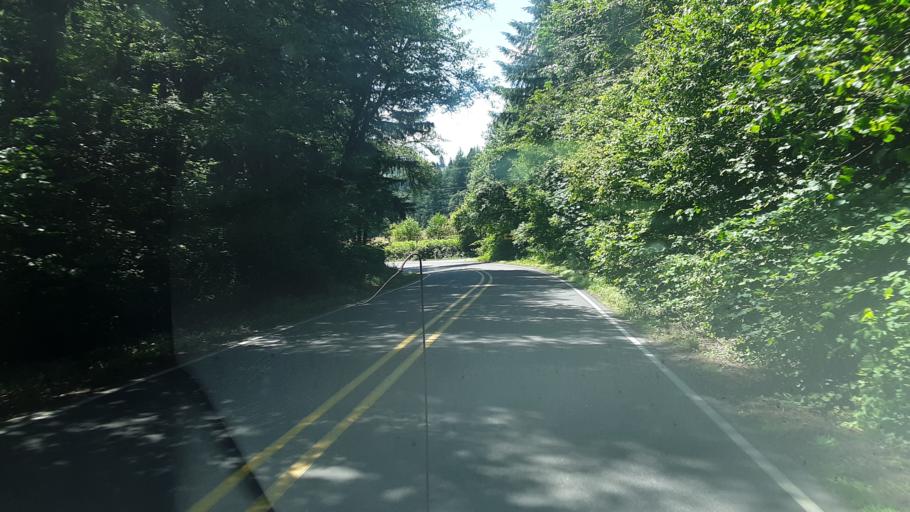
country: US
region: Washington
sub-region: Clark County
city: Amboy
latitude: 45.9064
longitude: -122.4506
